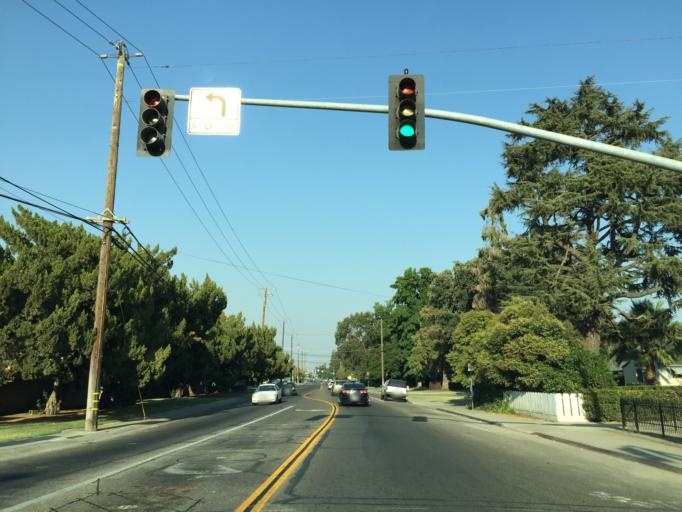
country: US
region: California
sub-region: Tulare County
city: Visalia
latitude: 36.3200
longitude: -119.3054
